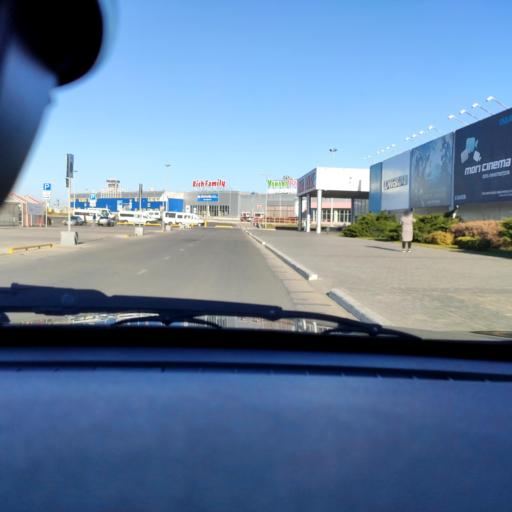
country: RU
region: Samara
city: Tol'yatti
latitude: 53.5420
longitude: 49.3884
